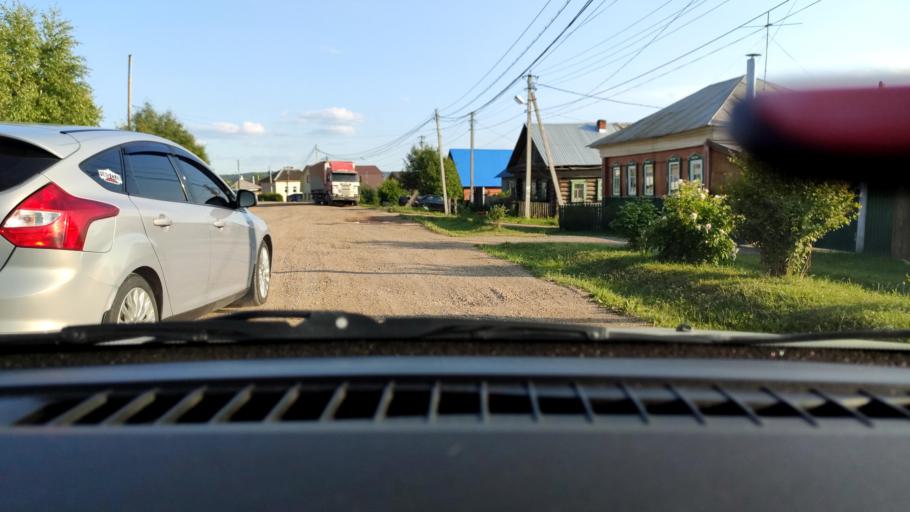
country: RU
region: Perm
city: Zvezdnyy
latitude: 57.7950
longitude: 56.3171
